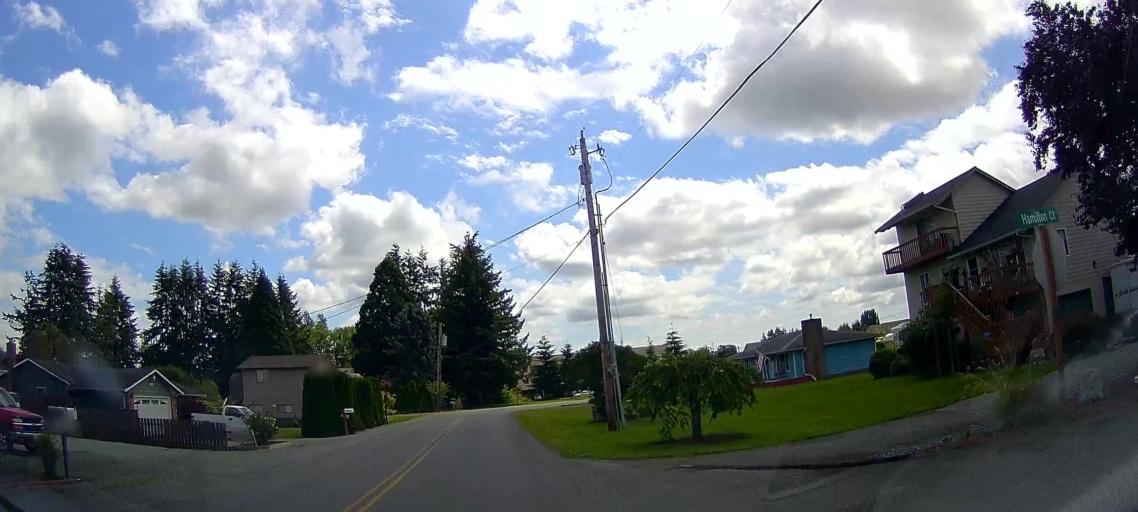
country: US
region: Washington
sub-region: Skagit County
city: Burlington
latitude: 48.4795
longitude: -122.3030
